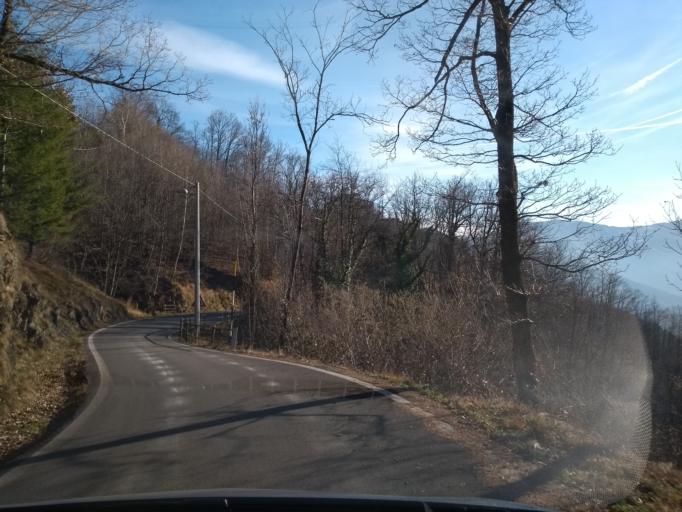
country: IT
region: Piedmont
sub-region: Provincia di Torino
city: Traves
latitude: 45.2827
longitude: 7.4370
